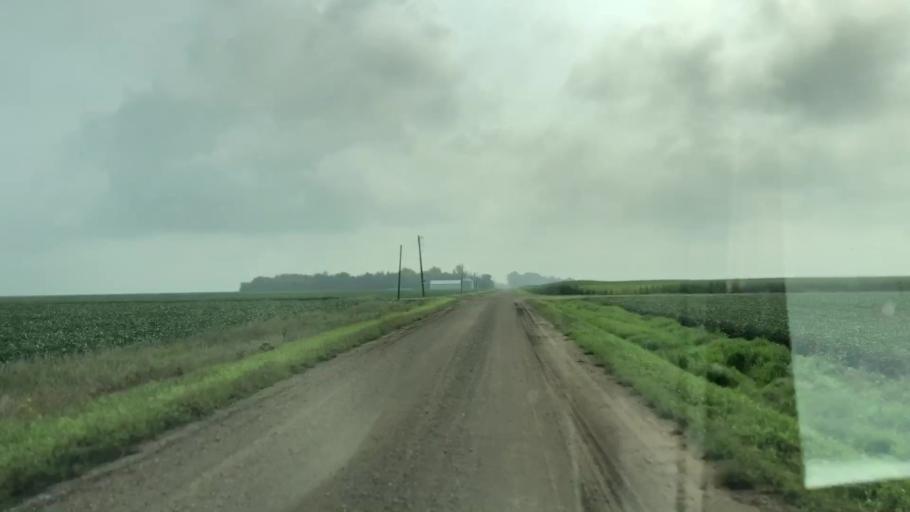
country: US
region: Iowa
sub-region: Sioux County
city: Hull
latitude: 43.2298
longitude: -96.0418
